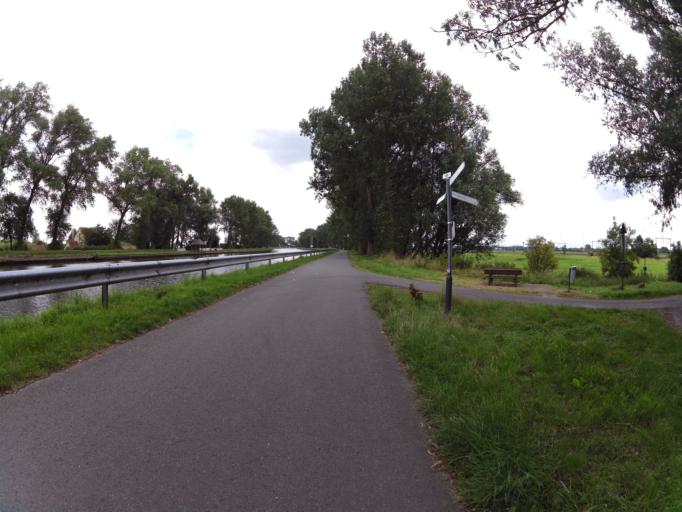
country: BE
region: Flanders
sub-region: Provincie West-Vlaanderen
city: Oudenburg
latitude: 51.2006
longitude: 3.0394
